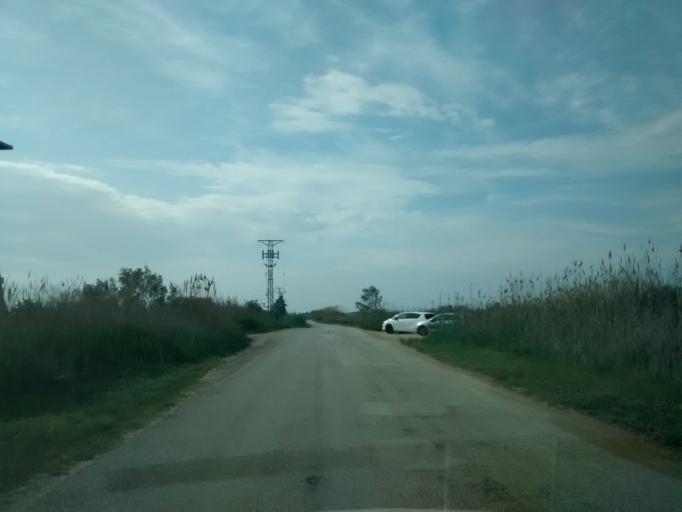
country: ES
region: Catalonia
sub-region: Provincia de Tarragona
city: Deltebre
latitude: 40.6869
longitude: 0.8502
